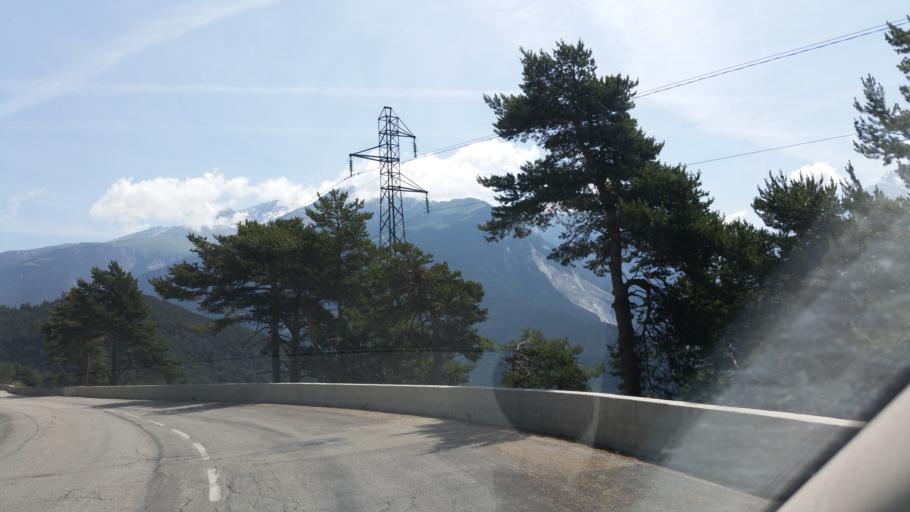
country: FR
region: Rhone-Alpes
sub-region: Departement de la Savoie
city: Modane
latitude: 45.2322
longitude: 6.7589
